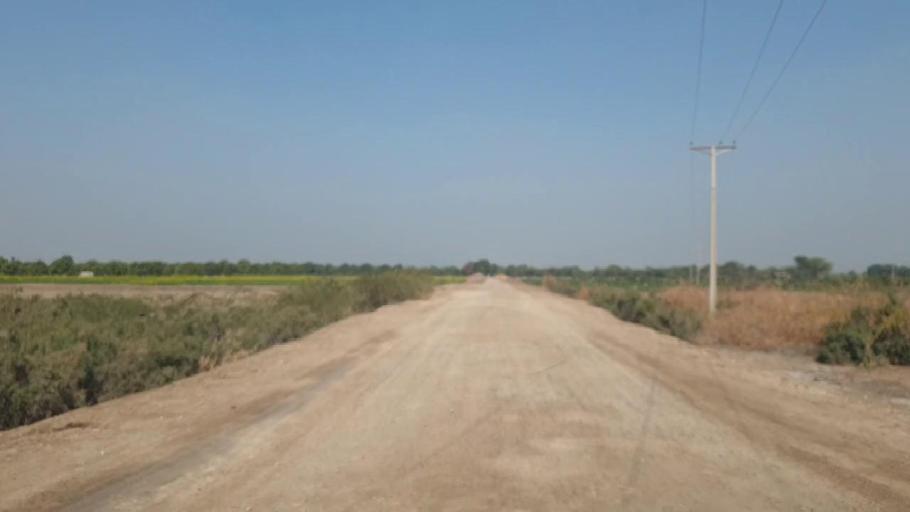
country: PK
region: Sindh
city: Mirwah Gorchani
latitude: 25.3799
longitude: 68.9317
